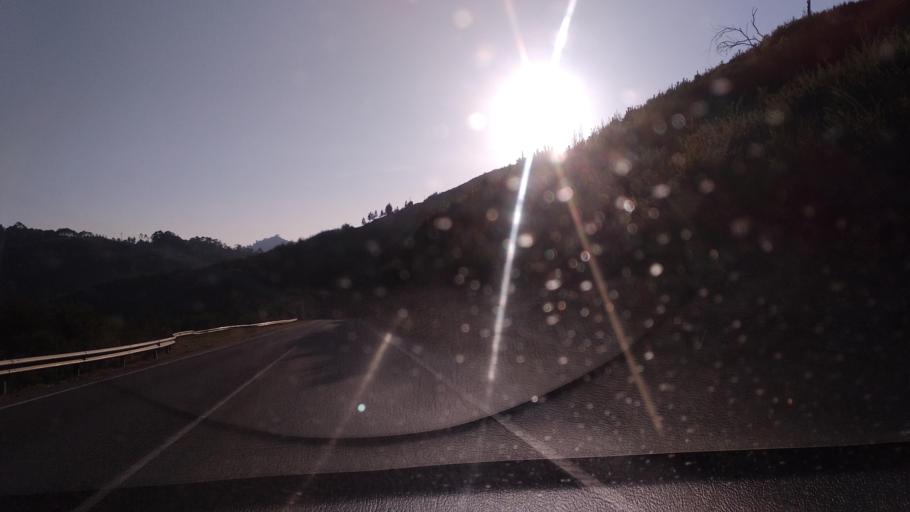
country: ES
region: Galicia
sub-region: Provincia de Pontevedra
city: Ponte Caldelas
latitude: 42.3413
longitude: -8.5448
